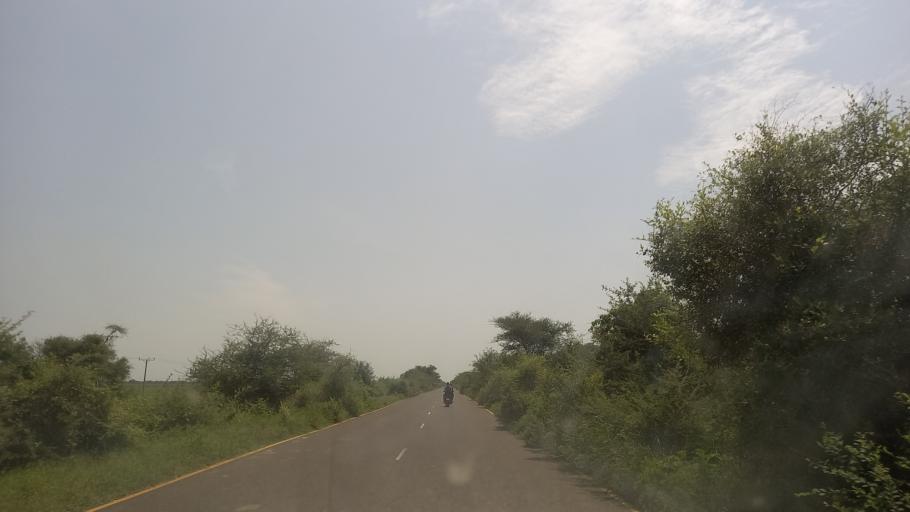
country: ET
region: Gambela
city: Gambela
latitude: 8.2837
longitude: 34.2164
